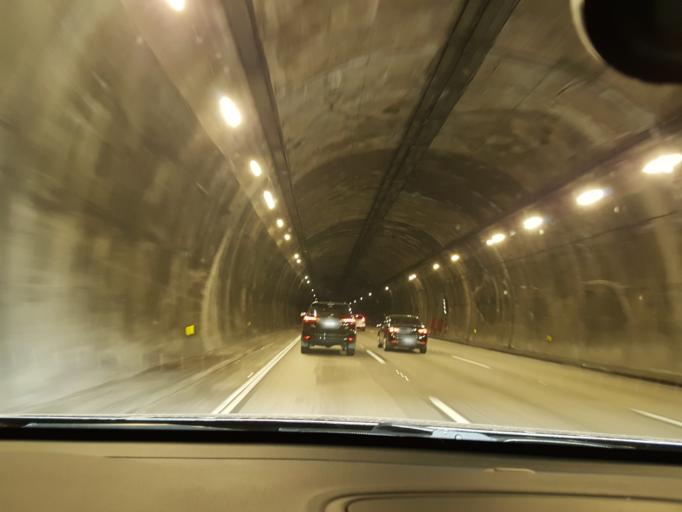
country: BR
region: Sao Paulo
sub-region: Cubatao
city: Cubatao
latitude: -23.8831
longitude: -46.4946
